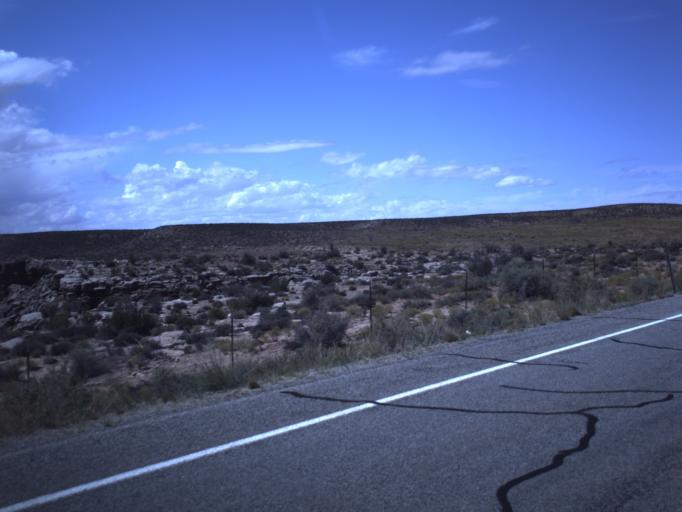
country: US
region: Utah
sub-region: San Juan County
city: Blanding
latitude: 37.2922
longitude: -109.4193
